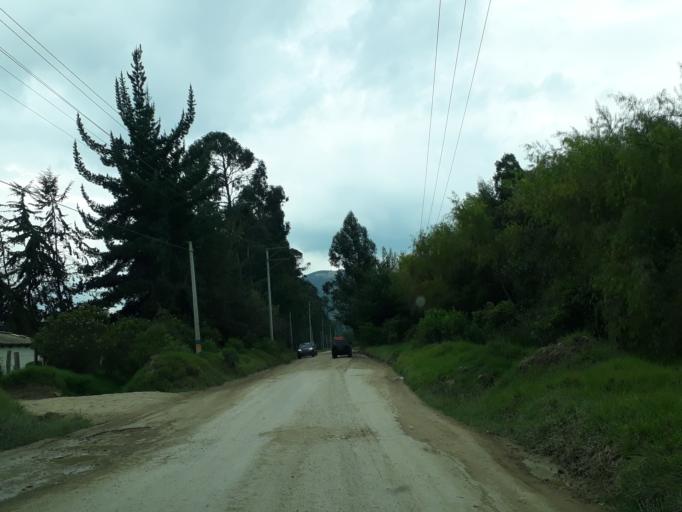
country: CO
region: Cundinamarca
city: Sesquile
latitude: 5.0669
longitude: -73.8143
